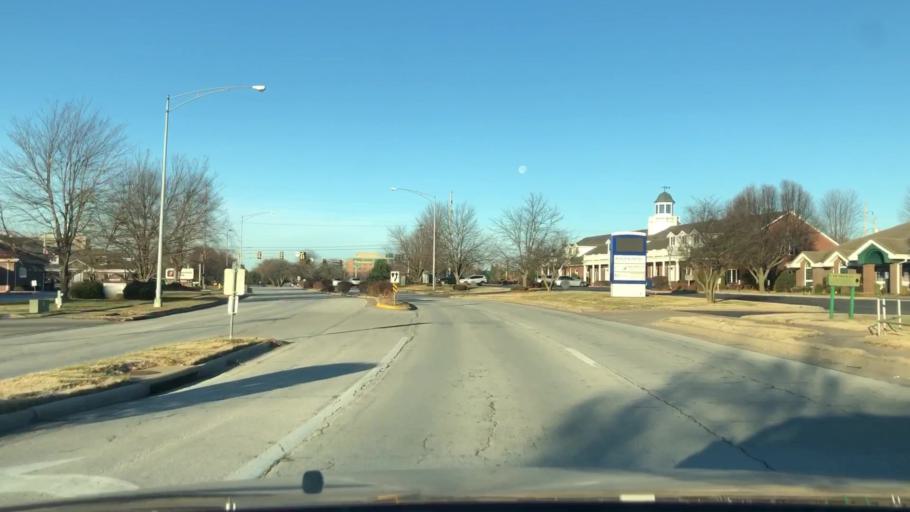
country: US
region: Missouri
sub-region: Greene County
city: Springfield
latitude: 37.1477
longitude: -93.2702
